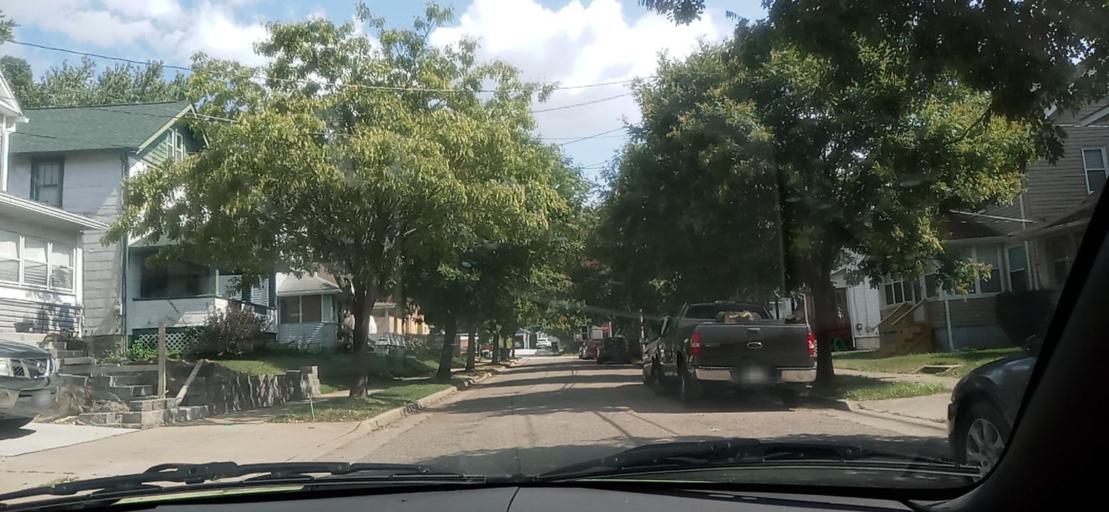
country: US
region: Ohio
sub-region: Summit County
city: Portage Lakes
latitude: 41.0407
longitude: -81.5595
